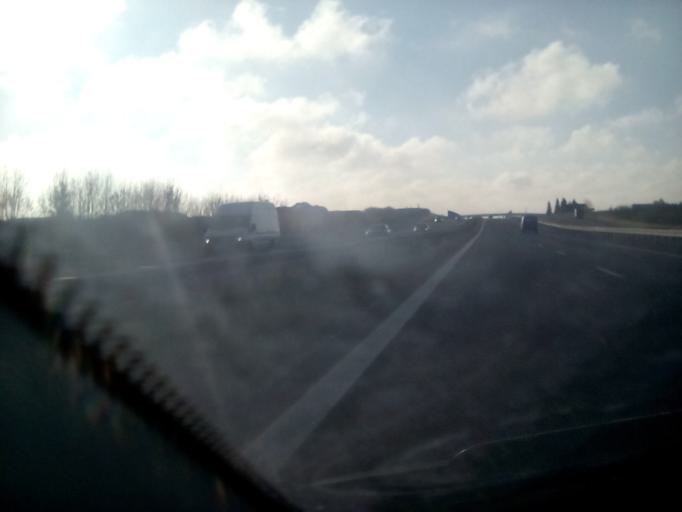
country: PL
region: Masovian Voivodeship
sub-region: Powiat grojecki
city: Jasieniec
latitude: 51.7951
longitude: 20.8909
